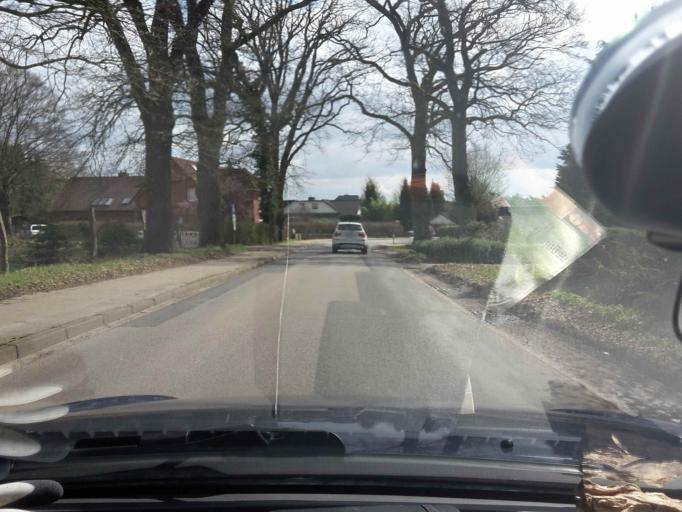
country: DE
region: Lower Saxony
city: Jesteburg
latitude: 53.3205
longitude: 9.9381
